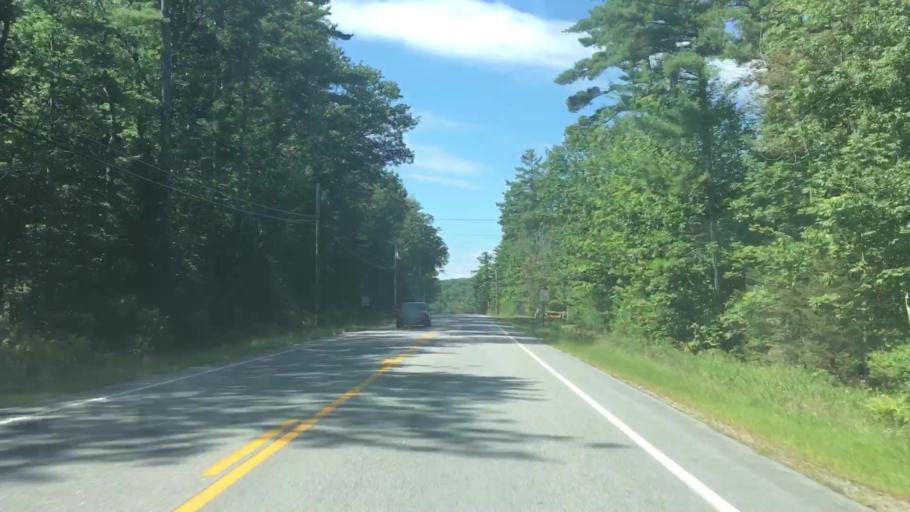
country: US
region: Maine
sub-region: Kennebec County
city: Monmouth
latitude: 44.1854
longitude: -69.9572
